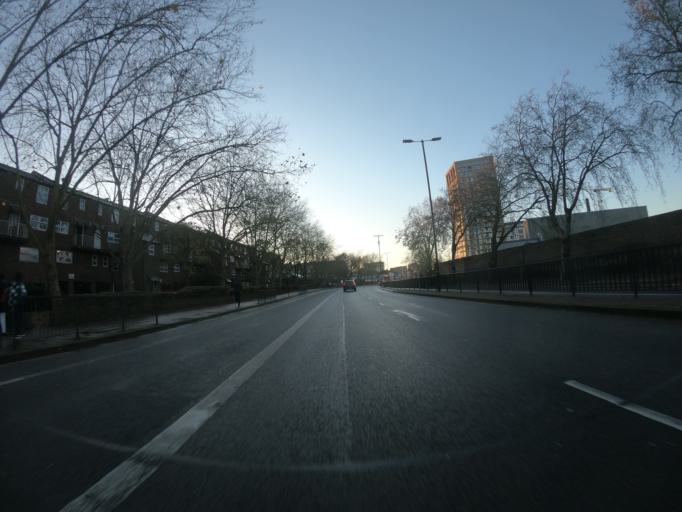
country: GB
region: England
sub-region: Greater London
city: Woolwich
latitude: 51.4908
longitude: 0.0755
